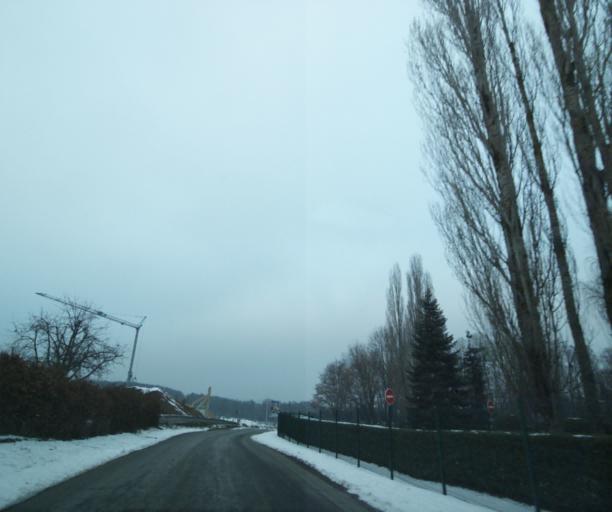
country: FR
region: Rhone-Alpes
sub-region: Departement de la Haute-Savoie
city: Reignier-Esery
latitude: 46.1436
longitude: 6.2383
